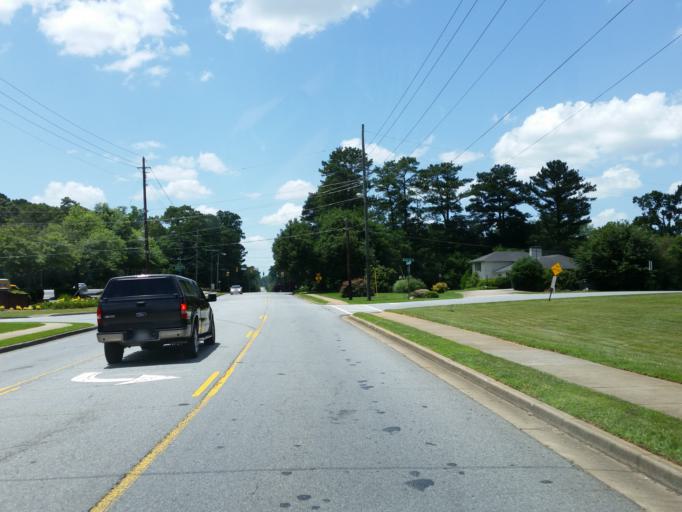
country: US
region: Georgia
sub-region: Cobb County
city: Smyrna
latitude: 33.9444
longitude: -84.4806
